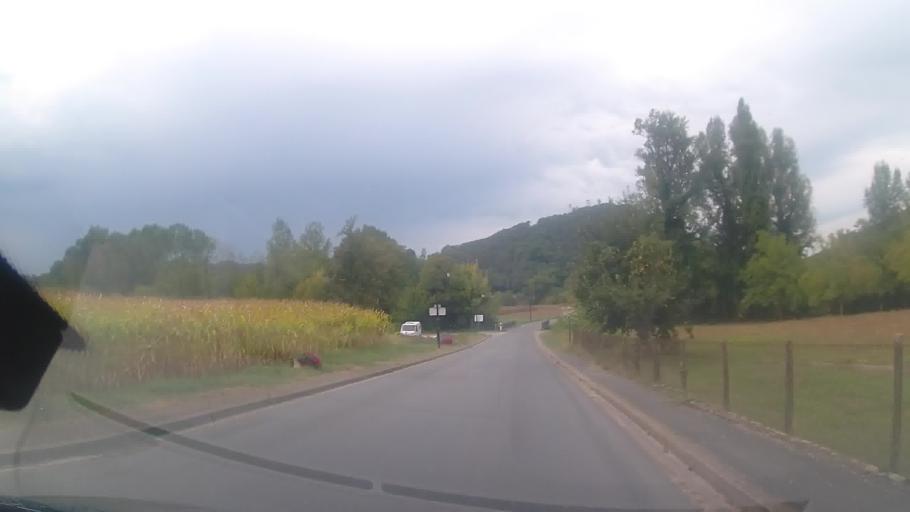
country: FR
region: Aquitaine
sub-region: Departement de la Dordogne
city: Eyvigues-et-Eybenes
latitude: 44.8614
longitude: 1.3614
